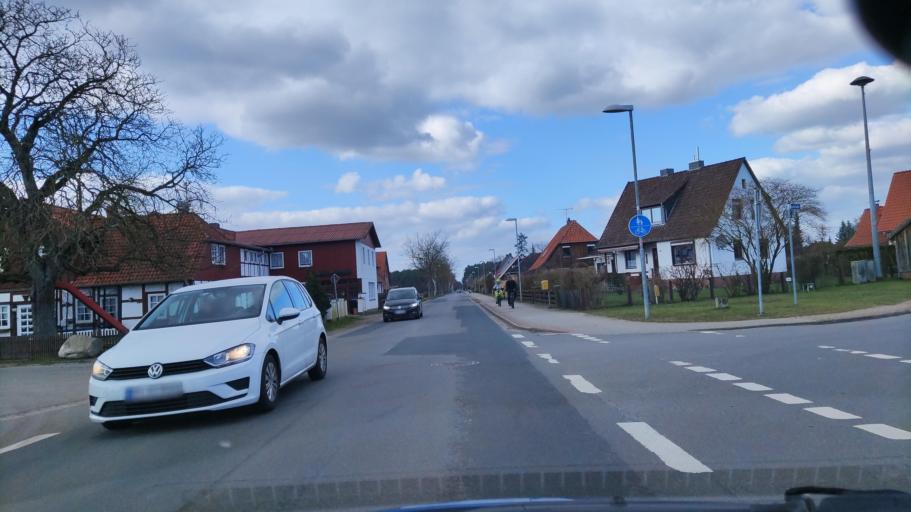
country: DE
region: Lower Saxony
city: Beedenbostel
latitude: 52.6360
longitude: 10.2157
